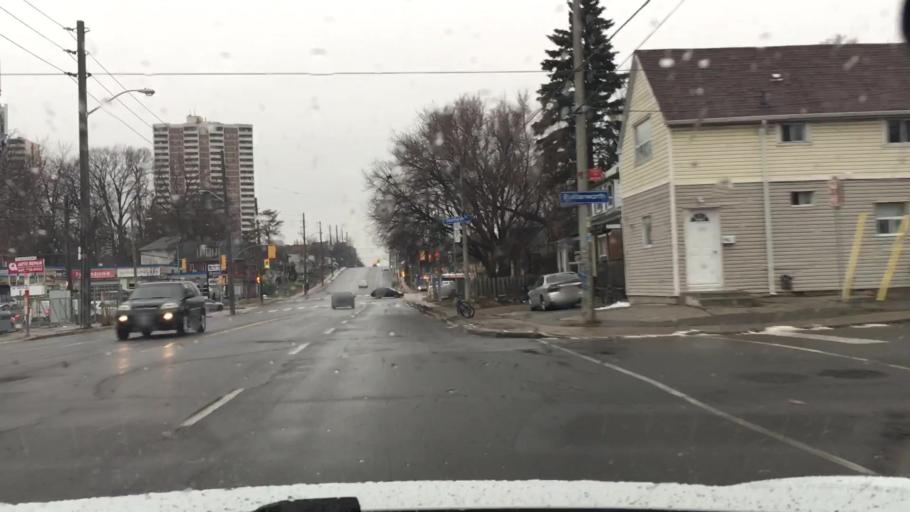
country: CA
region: Ontario
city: Scarborough
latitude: 43.6962
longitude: -79.2745
